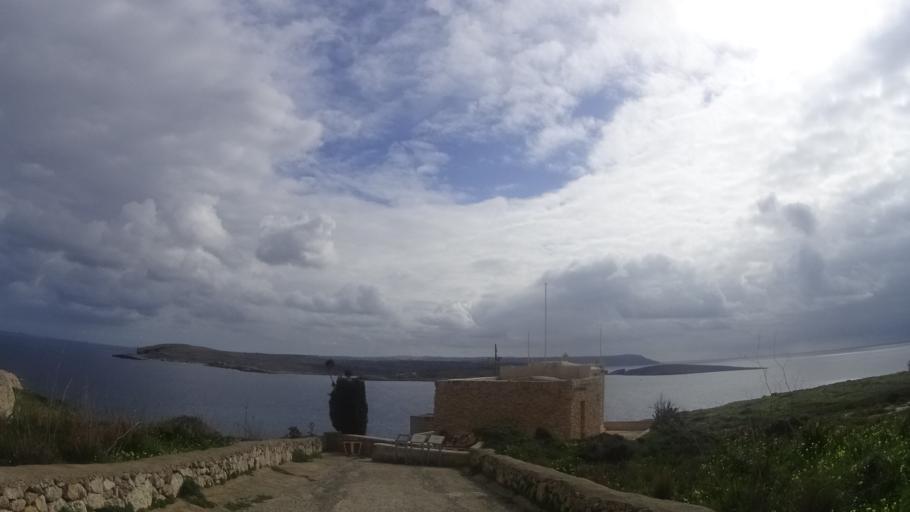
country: MT
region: Il-Qala
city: Qala
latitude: 36.0294
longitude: 14.3214
